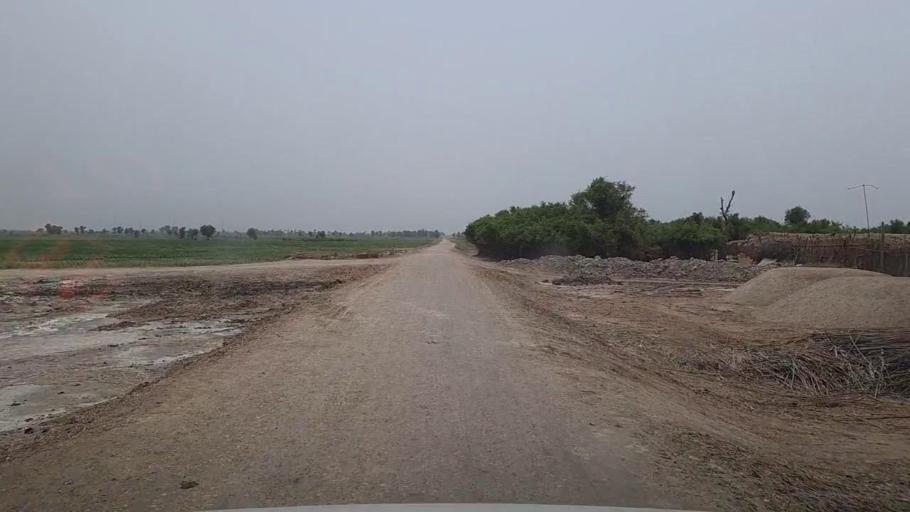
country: PK
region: Sindh
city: Sita Road
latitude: 27.0633
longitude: 67.8585
